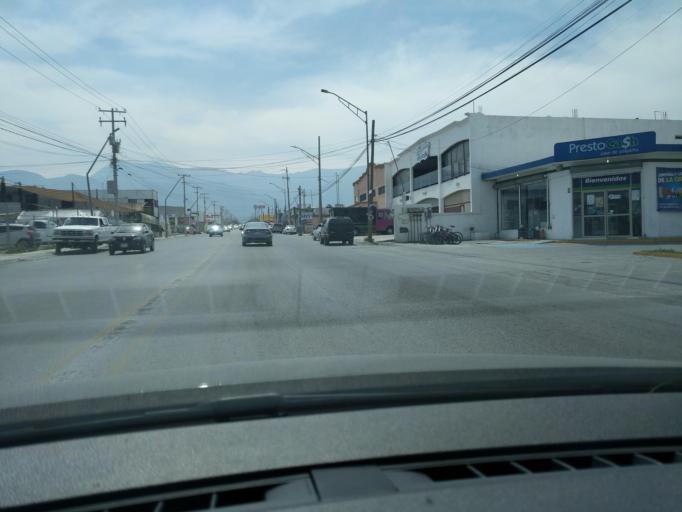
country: MX
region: Coahuila
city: Saltillo
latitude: 25.4279
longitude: -100.9465
